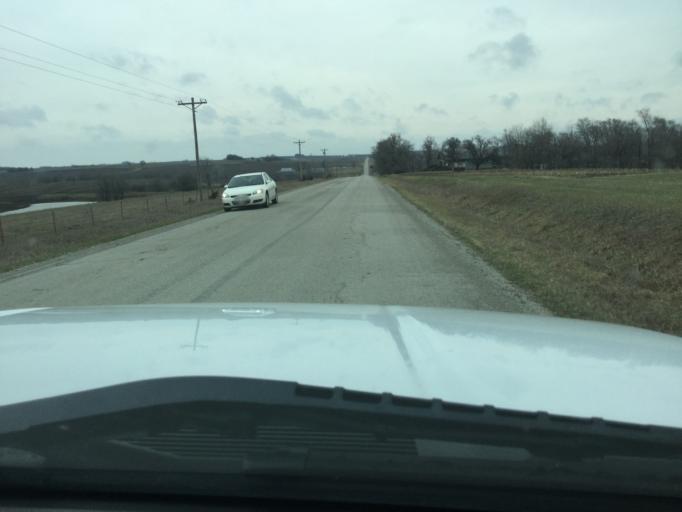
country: US
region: Kansas
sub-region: Nemaha County
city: Sabetha
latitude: 39.8721
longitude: -95.7139
